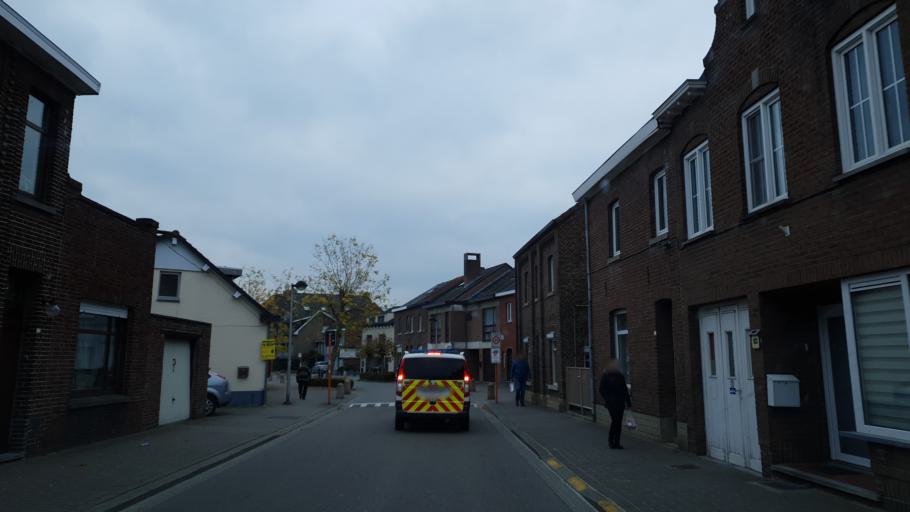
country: BE
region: Flanders
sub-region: Provincie Limburg
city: Lanaken
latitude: 50.8923
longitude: 5.6477
